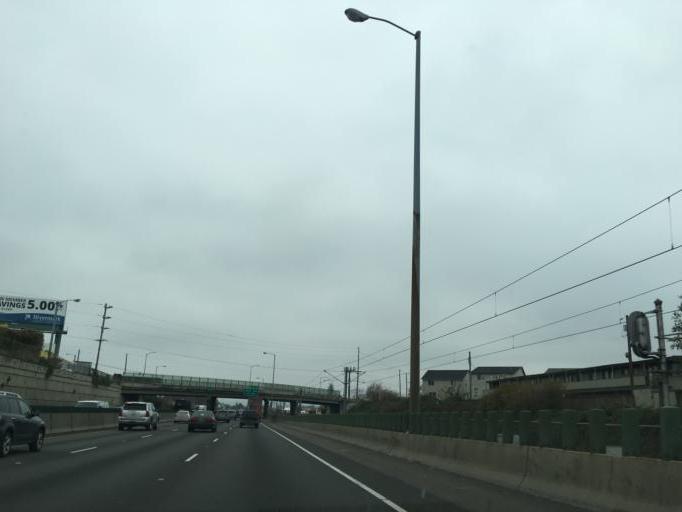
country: US
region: Oregon
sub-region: Multnomah County
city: Lents
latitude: 45.5348
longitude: -122.5915
